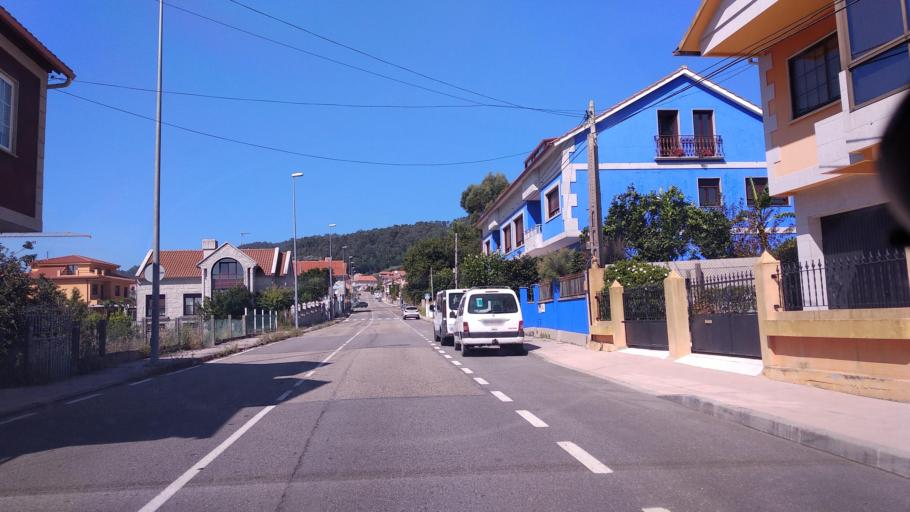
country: ES
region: Galicia
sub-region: Provincia de Pontevedra
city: Cangas
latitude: 42.2718
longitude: -8.7676
